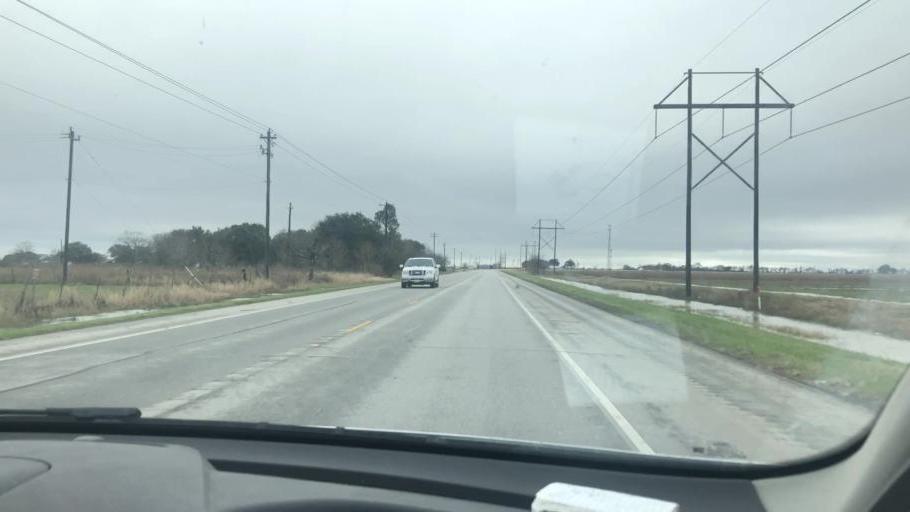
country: US
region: Texas
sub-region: Wharton County
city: Boling
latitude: 29.1490
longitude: -95.9891
